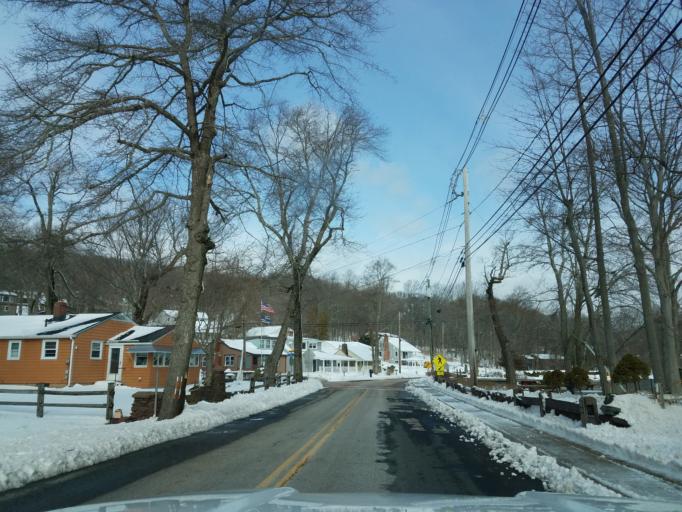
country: US
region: Connecticut
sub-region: Middlesex County
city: Lake Pocotopaug
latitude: 41.5999
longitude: -72.5112
